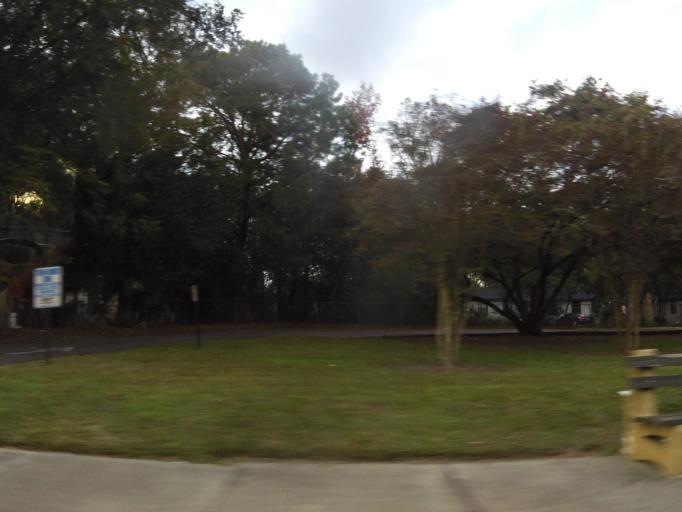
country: US
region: Florida
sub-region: Duval County
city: Jacksonville
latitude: 30.3367
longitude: -81.7147
